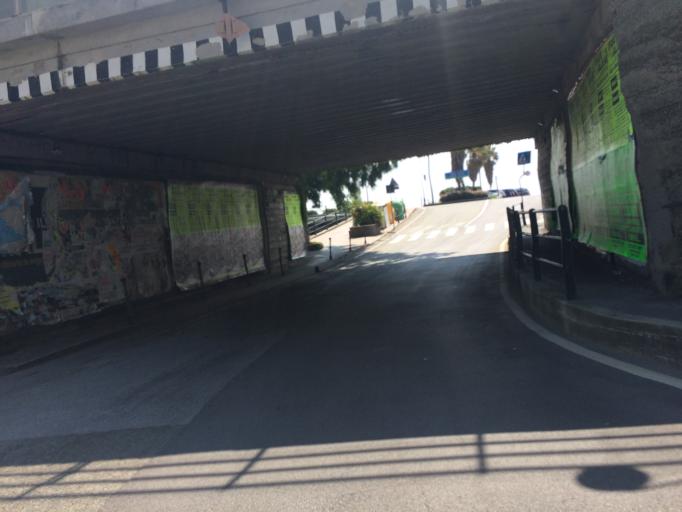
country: IT
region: Liguria
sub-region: Provincia di Genova
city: Cogoleto
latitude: 44.3865
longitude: 8.6386
